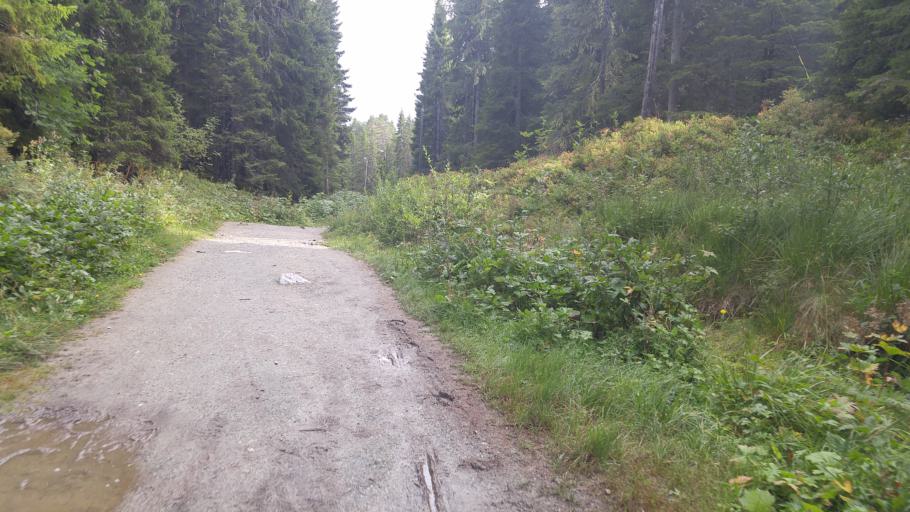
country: NO
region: Sor-Trondelag
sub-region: Trondheim
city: Trondheim
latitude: 63.4109
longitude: 10.3317
